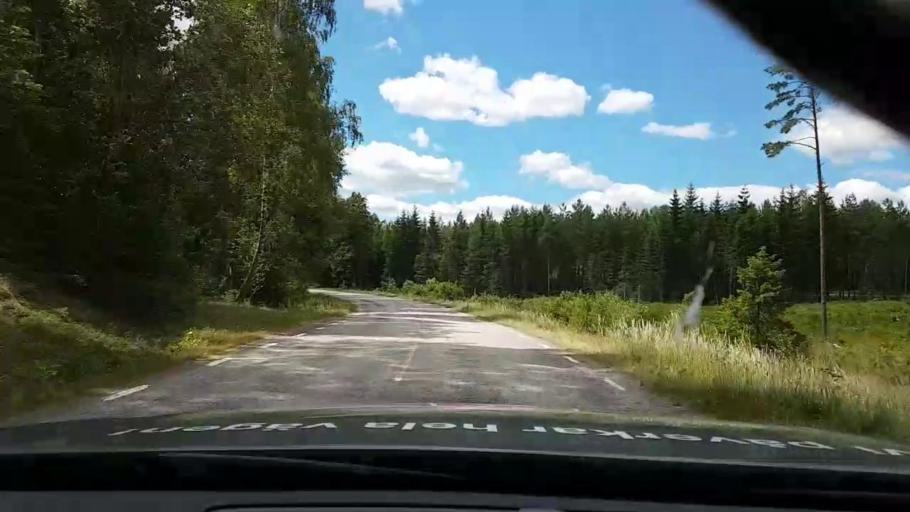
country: SE
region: Kalmar
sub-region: Vasterviks Kommun
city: Forserum
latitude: 58.0256
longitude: 16.5358
